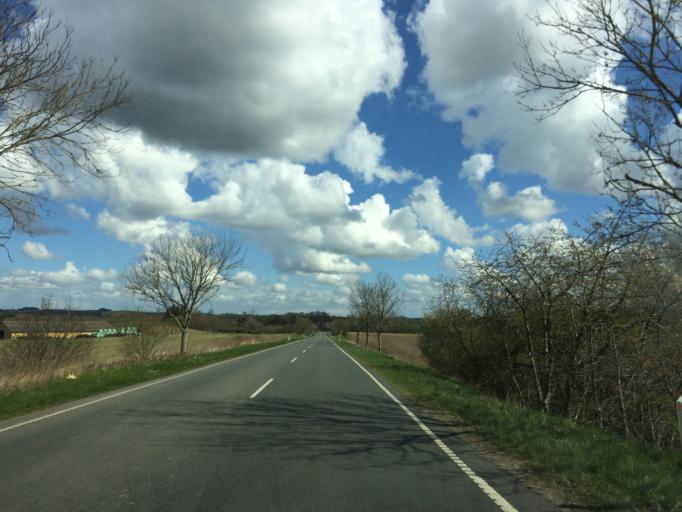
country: DK
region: South Denmark
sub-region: Assens Kommune
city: Harby
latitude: 55.2232
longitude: 10.1722
